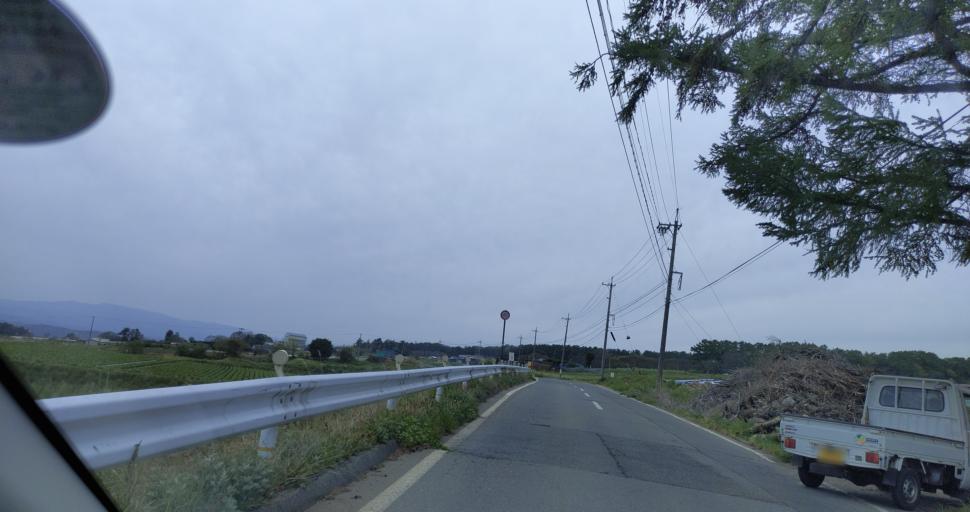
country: JP
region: Nagano
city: Komoro
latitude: 36.3367
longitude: 138.4807
